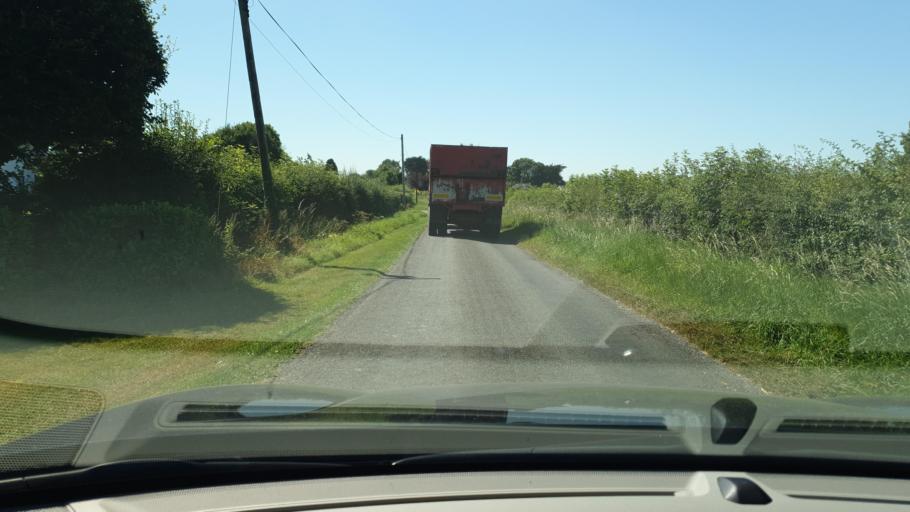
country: IE
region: Leinster
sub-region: An Mhi
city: Ashbourne
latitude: 53.4557
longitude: -6.4247
